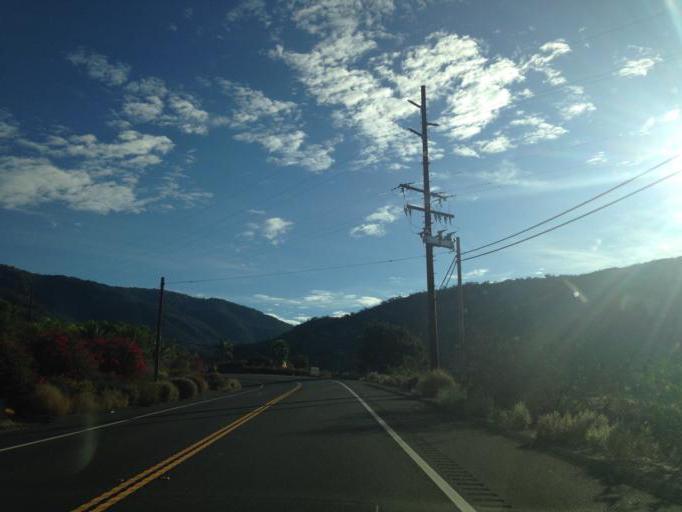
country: US
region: California
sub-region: San Diego County
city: Valley Center
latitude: 33.2987
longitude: -116.9409
